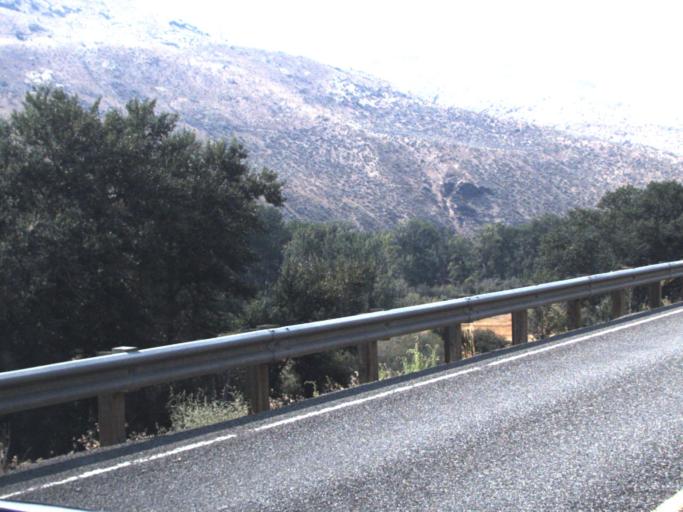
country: US
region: Washington
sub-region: Kittitas County
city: Ellensburg
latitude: 46.9070
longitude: -120.4997
